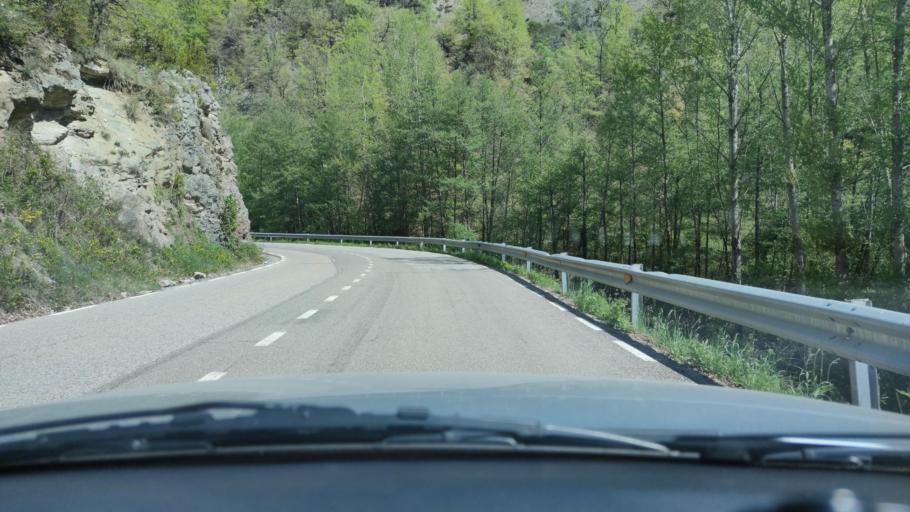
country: ES
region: Catalonia
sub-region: Provincia de Lleida
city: Coll de Nargo
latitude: 42.3148
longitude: 1.2882
